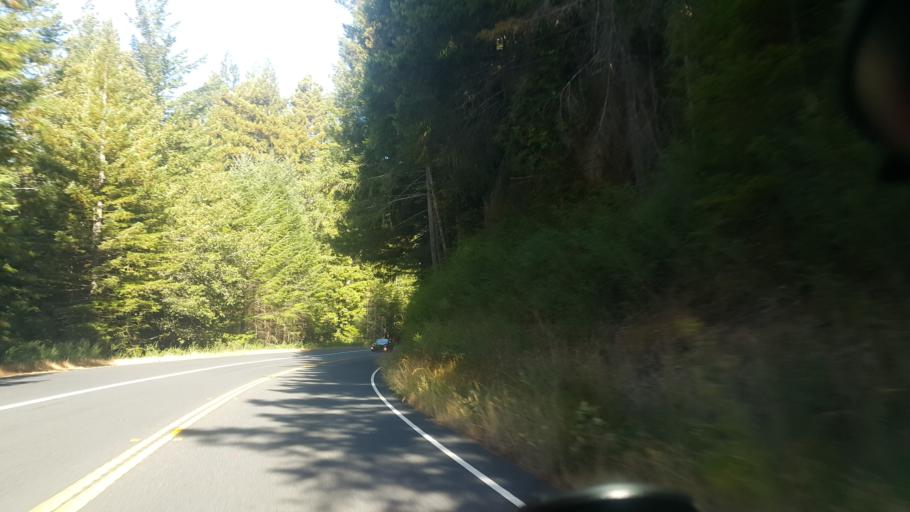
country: US
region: California
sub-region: Mendocino County
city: Fort Bragg
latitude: 39.3618
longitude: -123.6633
